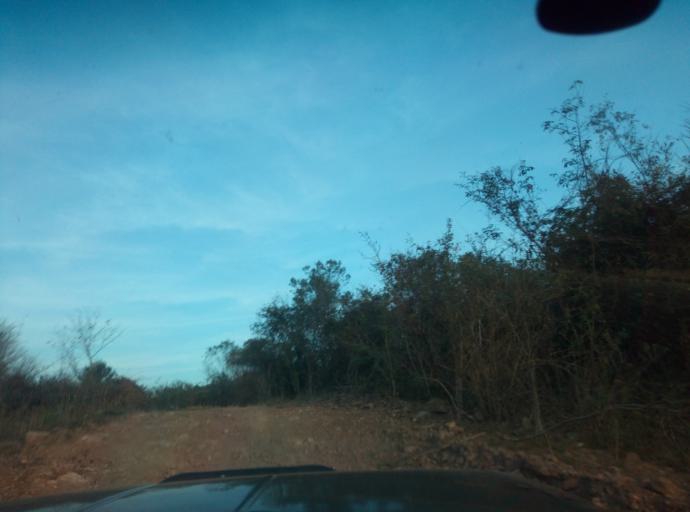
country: PY
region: Caaguazu
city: Yhu
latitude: -25.1995
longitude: -56.1101
